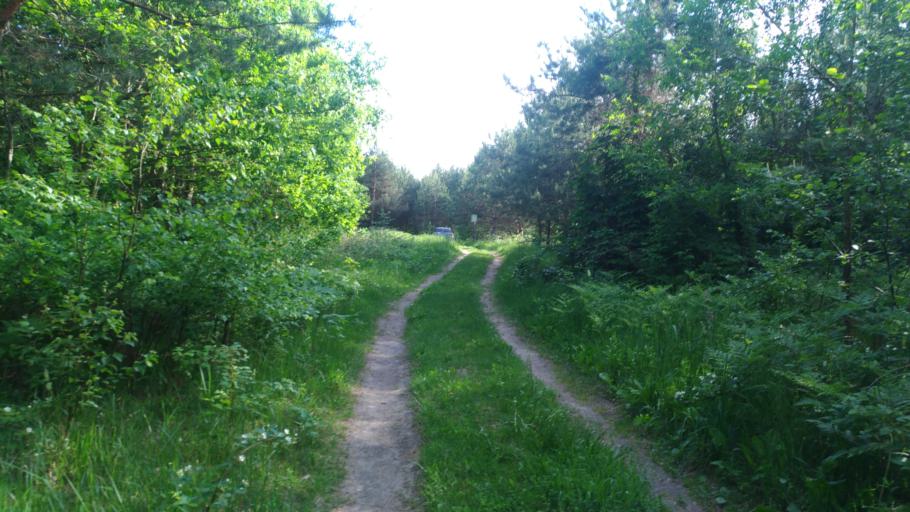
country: LT
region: Kauno apskritis
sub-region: Kauno rajonas
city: Karmelava
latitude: 54.9883
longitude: 24.1112
